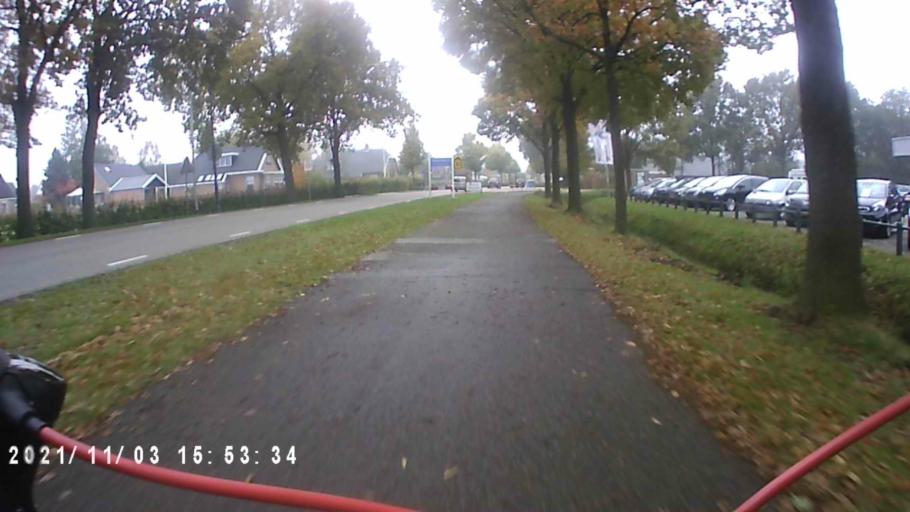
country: NL
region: Groningen
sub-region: Gemeente Leek
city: Leek
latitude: 53.0709
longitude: 6.3322
